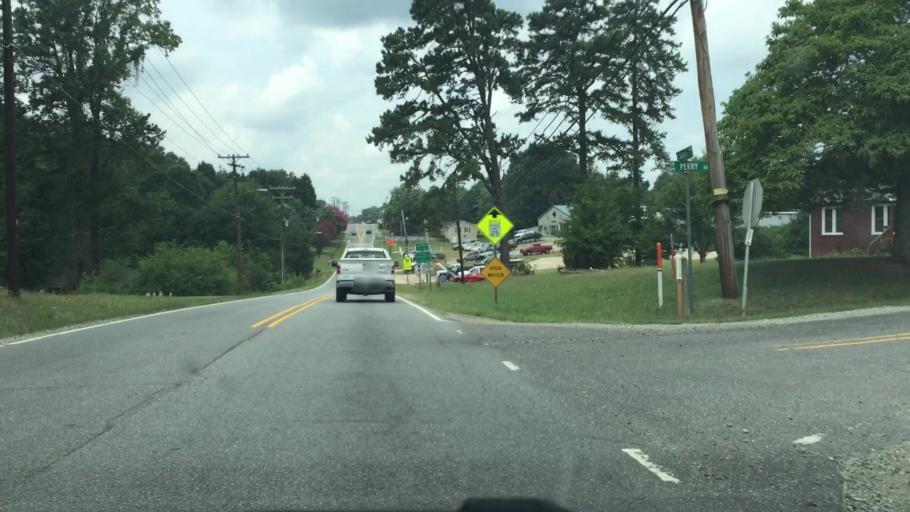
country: US
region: North Carolina
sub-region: Iredell County
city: Troutman
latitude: 35.6978
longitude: -80.8799
